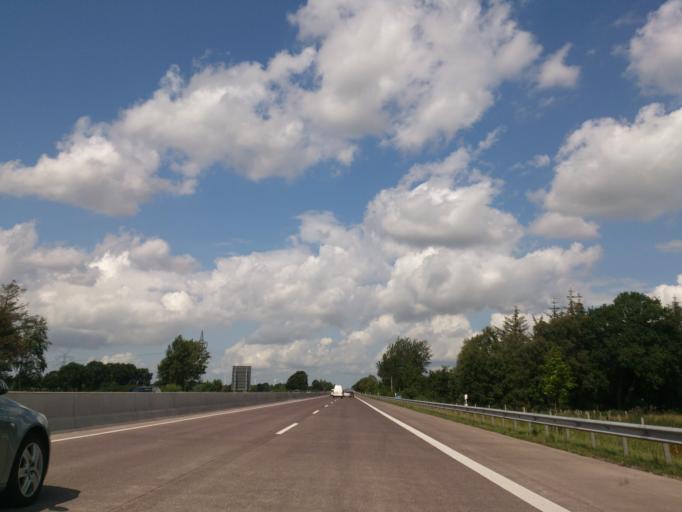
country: DE
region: Schleswig-Holstein
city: Klein Offenseth-Sparrieshoop
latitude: 53.8123
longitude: 9.6658
